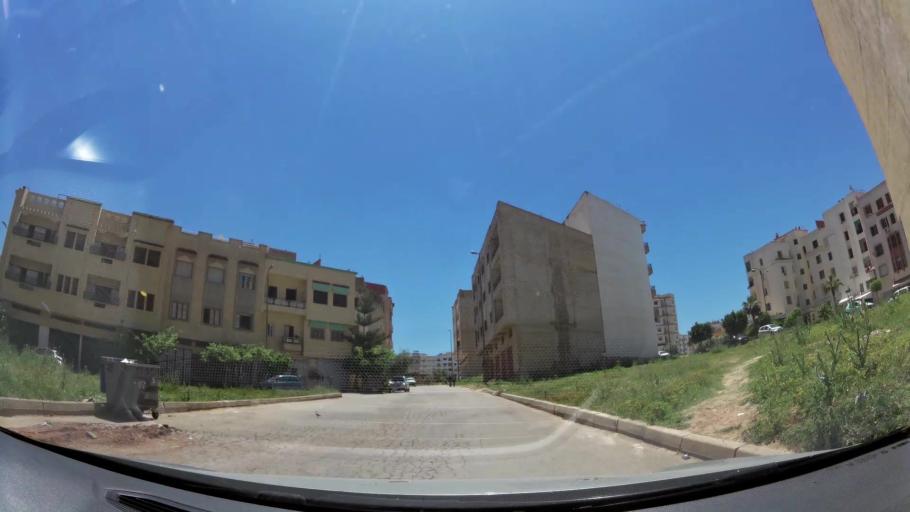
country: MA
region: Meknes-Tafilalet
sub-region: Meknes
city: Meknes
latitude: 33.8651
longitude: -5.5761
